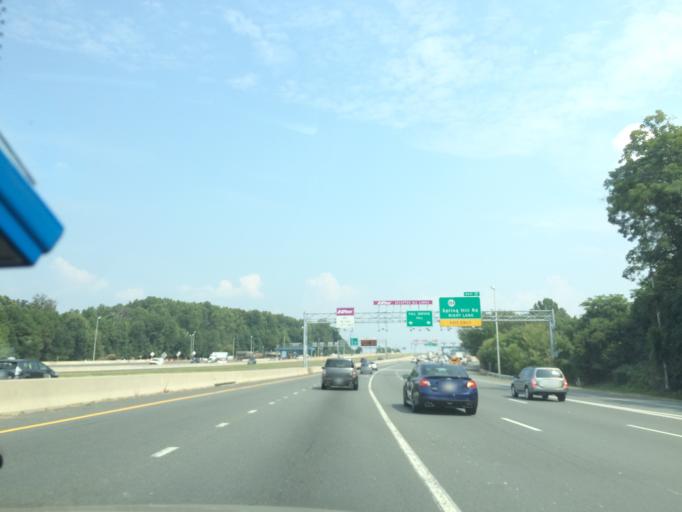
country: US
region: Virginia
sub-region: Fairfax County
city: Tysons Corner
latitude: 38.9345
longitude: -77.2431
